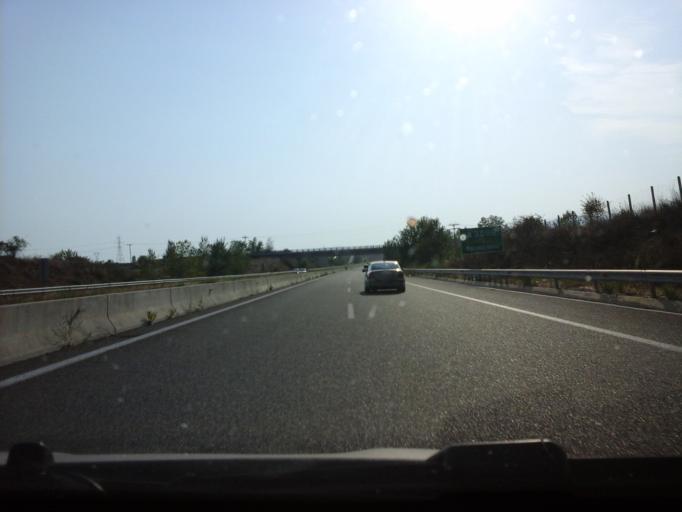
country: GR
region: East Macedonia and Thrace
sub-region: Nomos Xanthis
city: Petrochori
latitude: 41.0612
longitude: 24.8367
